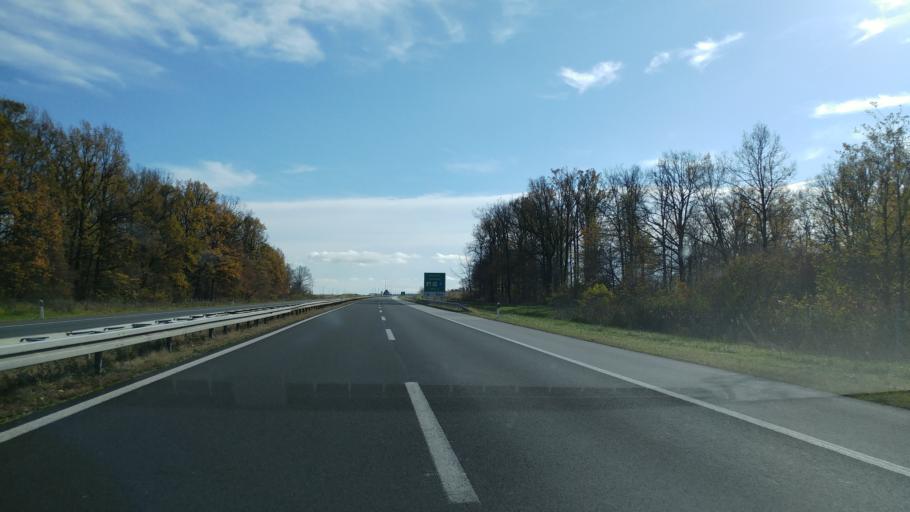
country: HR
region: Sisacko-Moslavacka
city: Lipovljani
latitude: 45.4122
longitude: 16.8527
